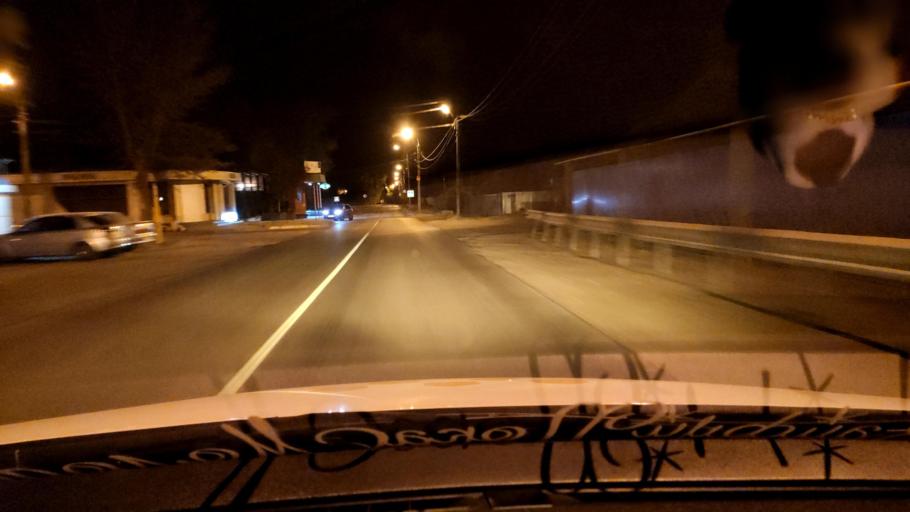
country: RU
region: Voronezj
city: Pridonskoy
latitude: 51.6877
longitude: 39.0798
